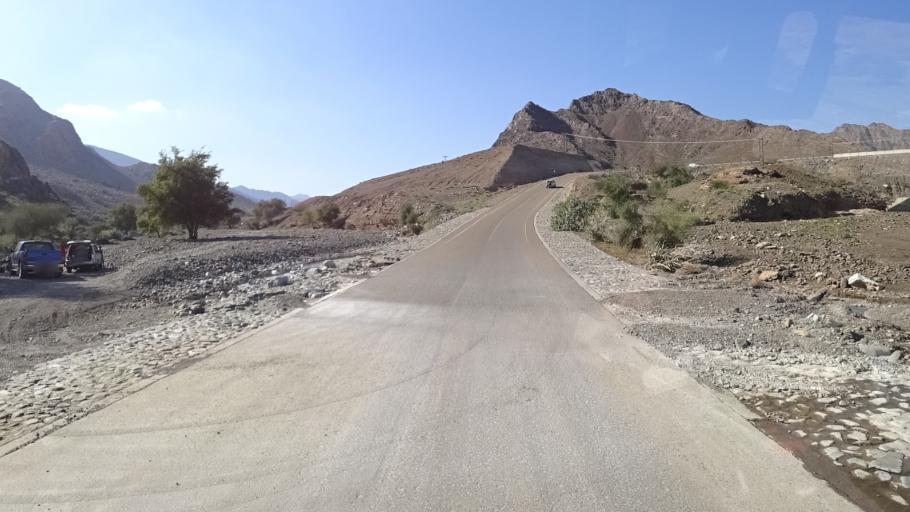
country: OM
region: Al Batinah
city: Rustaq
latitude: 23.4580
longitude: 57.0835
